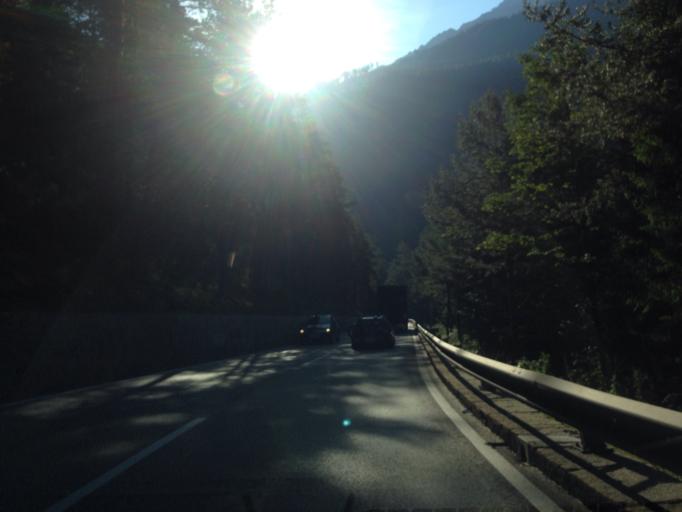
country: AT
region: Tyrol
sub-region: Politischer Bezirk Imst
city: Nassereith
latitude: 47.3544
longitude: 10.8380
